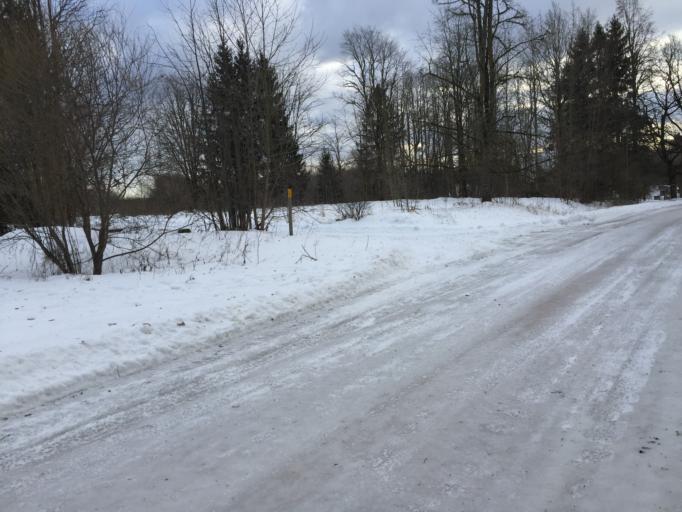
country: LV
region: Lielvarde
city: Lielvarde
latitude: 56.5774
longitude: 24.7368
